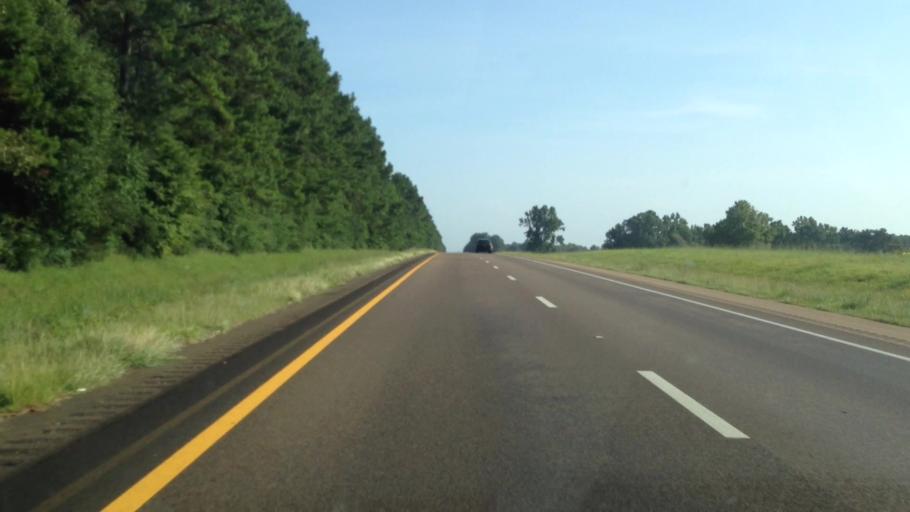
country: US
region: Mississippi
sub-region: Pike County
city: Summit
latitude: 31.3081
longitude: -90.4778
